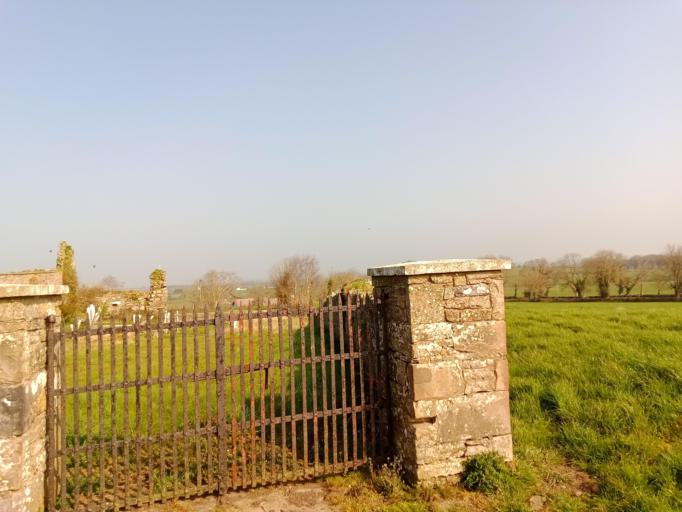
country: IE
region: Leinster
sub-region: Kilkenny
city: Callan
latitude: 52.5017
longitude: -7.3841
